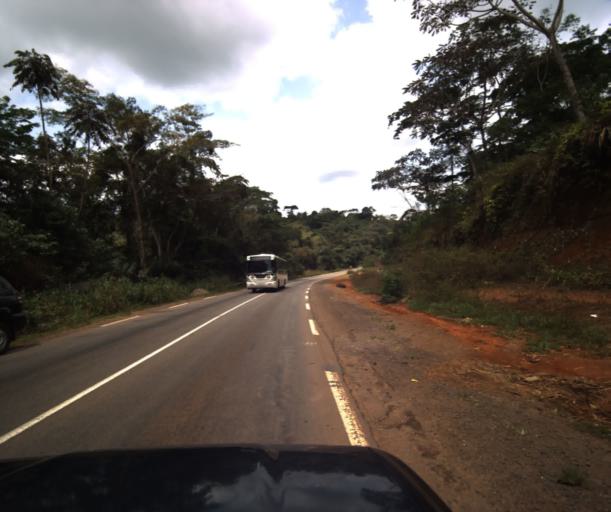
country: CM
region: Centre
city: Mbankomo
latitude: 3.7866
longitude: 11.3159
